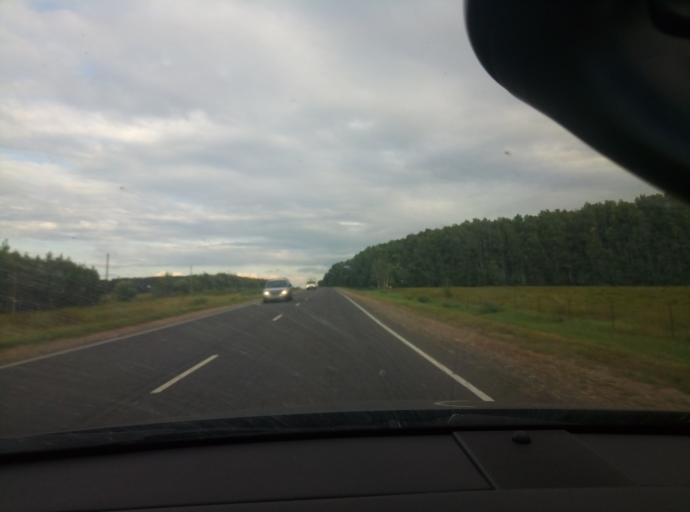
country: RU
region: Tula
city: Dubna
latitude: 54.3324
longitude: 36.9083
